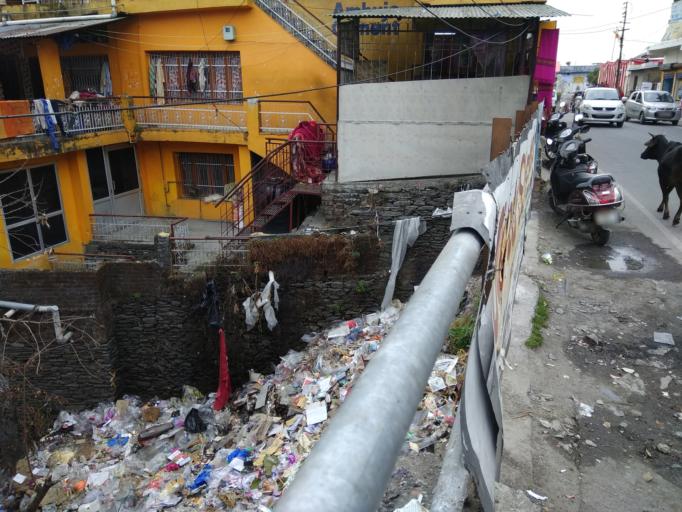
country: IN
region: Himachal Pradesh
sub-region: Kangra
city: Dharmsala
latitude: 32.1835
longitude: 76.3740
